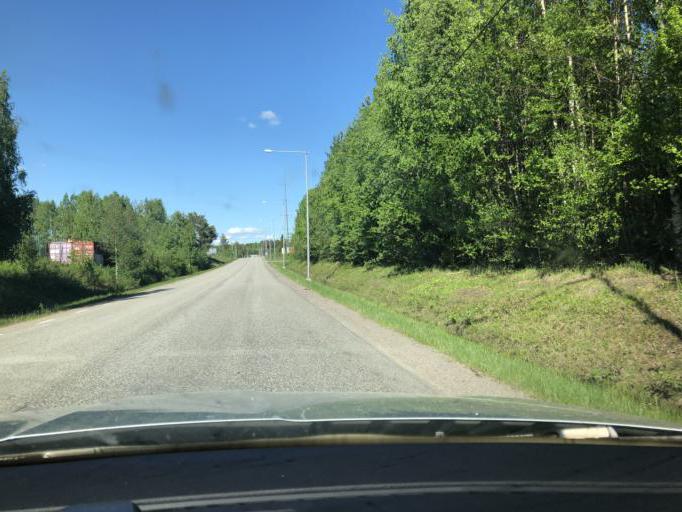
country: SE
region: Norrbotten
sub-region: Kalix Kommun
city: Kalix
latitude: 65.8677
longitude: 23.1431
